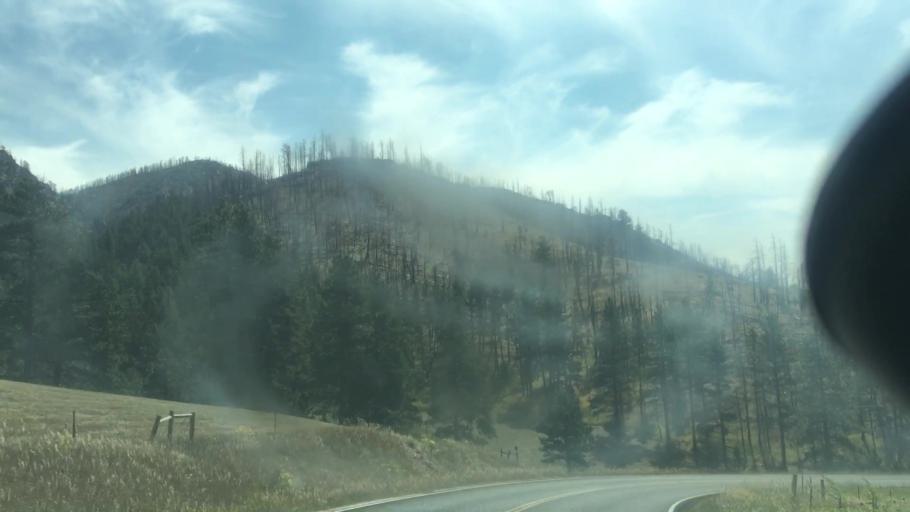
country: US
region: Colorado
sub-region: Larimer County
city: Laporte
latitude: 40.5907
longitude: -105.3365
